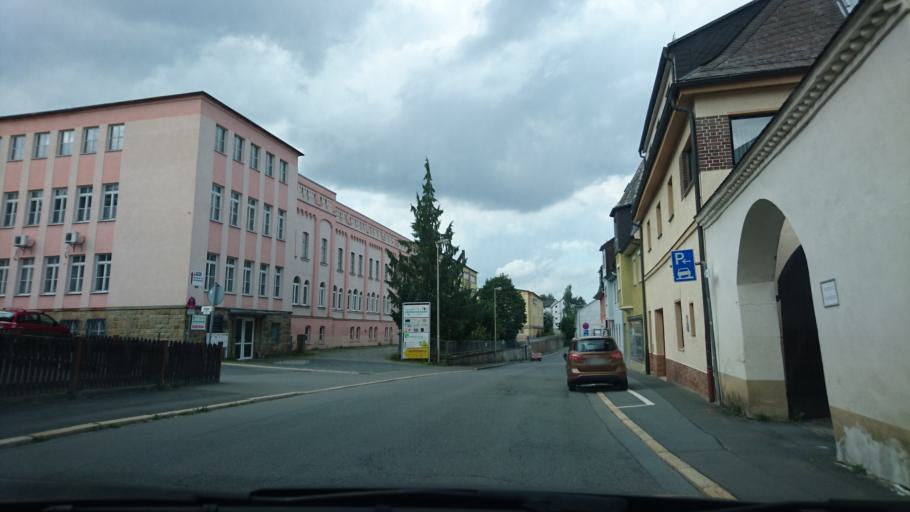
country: DE
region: Bavaria
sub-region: Upper Franconia
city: Naila
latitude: 50.3325
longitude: 11.7070
